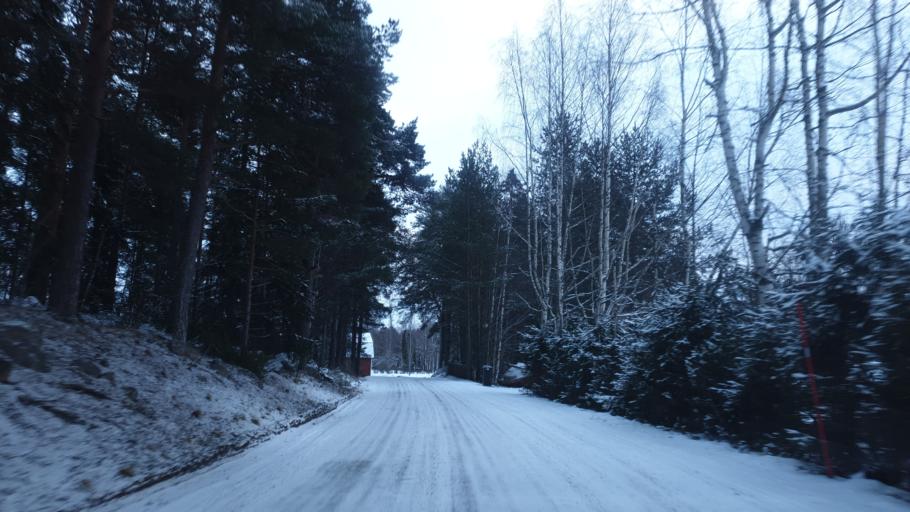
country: SE
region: Gaevleborg
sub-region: Bollnas Kommun
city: Kilafors
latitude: 61.2545
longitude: 16.5425
